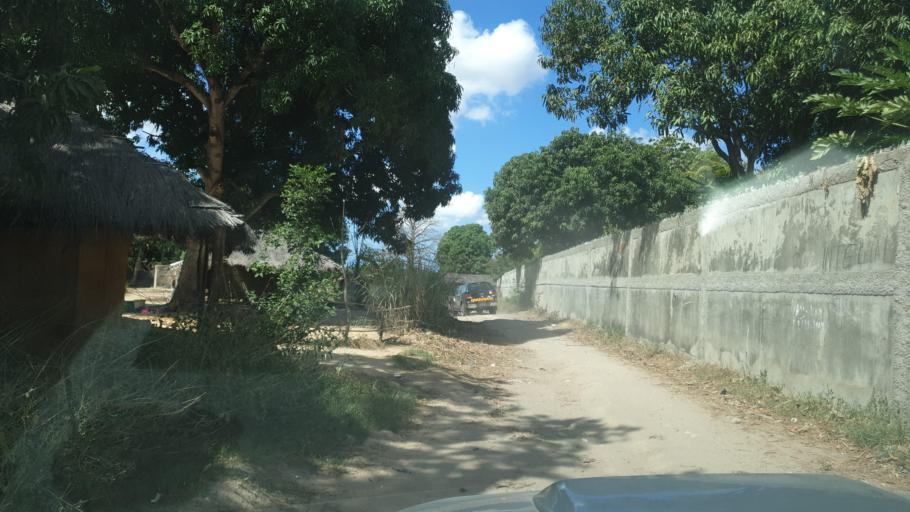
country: MZ
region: Nampula
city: Nacala
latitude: -14.5678
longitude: 40.7022
